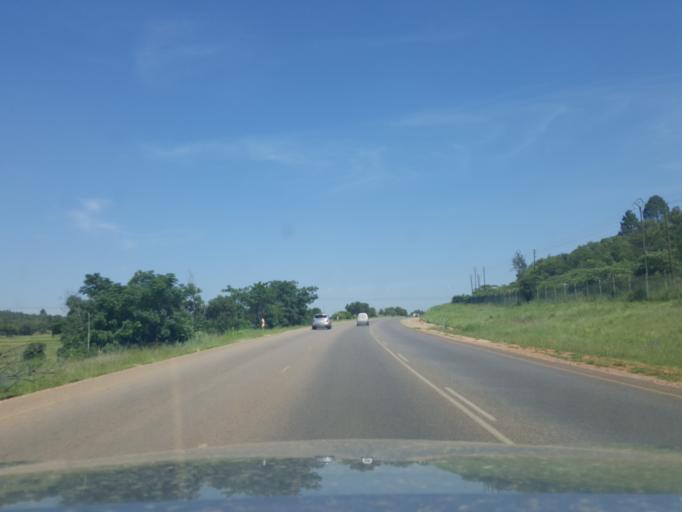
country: ZA
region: Gauteng
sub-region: City of Tshwane Metropolitan Municipality
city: Cullinan
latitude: -25.6776
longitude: 28.3495
